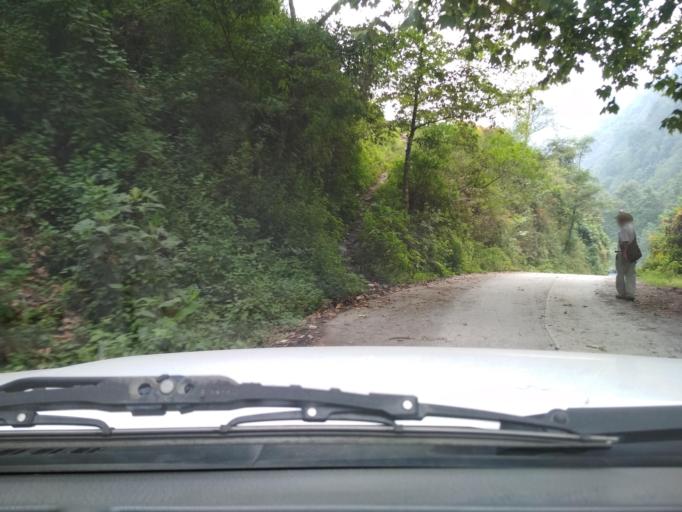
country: MX
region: Veracruz
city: Xocotla
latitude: 18.9894
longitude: -97.1107
